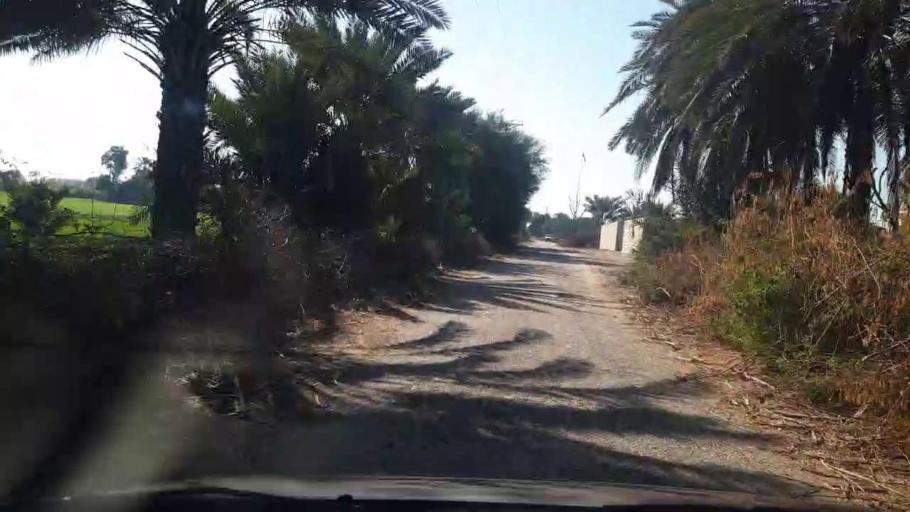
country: PK
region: Sindh
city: Bozdar
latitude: 27.2613
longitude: 68.6531
